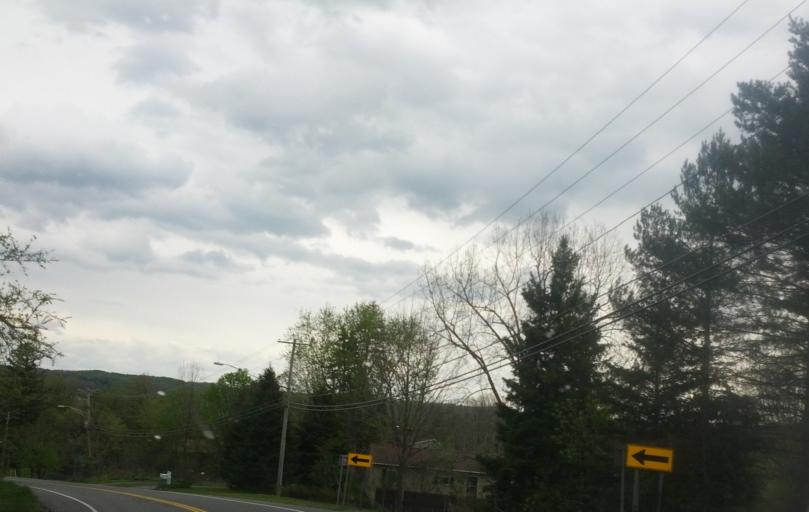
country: US
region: New York
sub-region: Onondaga County
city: Manlius
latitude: 42.9920
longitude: -75.9934
